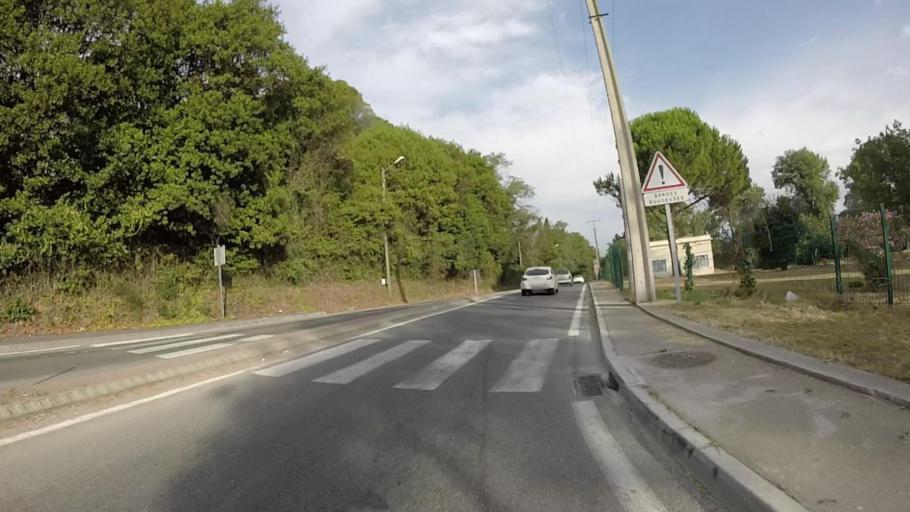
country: FR
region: Provence-Alpes-Cote d'Azur
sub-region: Departement des Alpes-Maritimes
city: Biot
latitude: 43.6152
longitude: 7.1083
